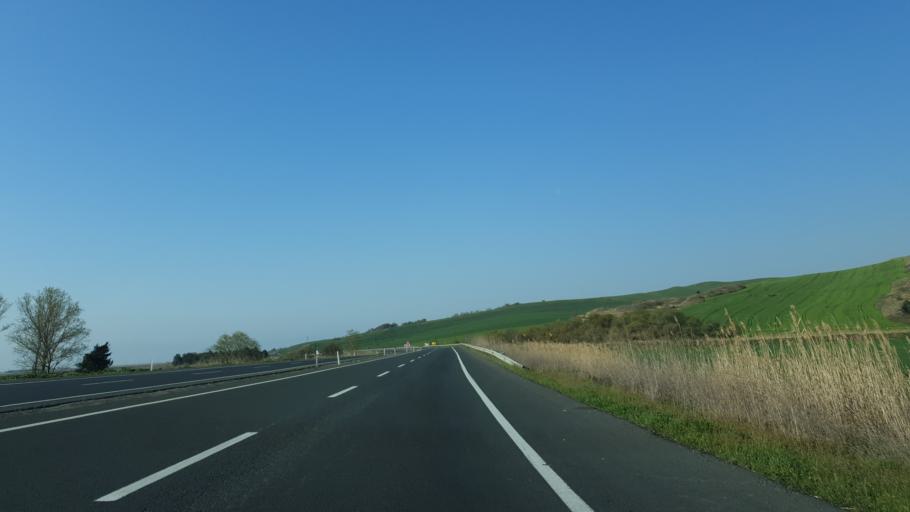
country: TR
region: Tekirdag
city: Corlu
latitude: 41.0528
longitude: 27.7367
